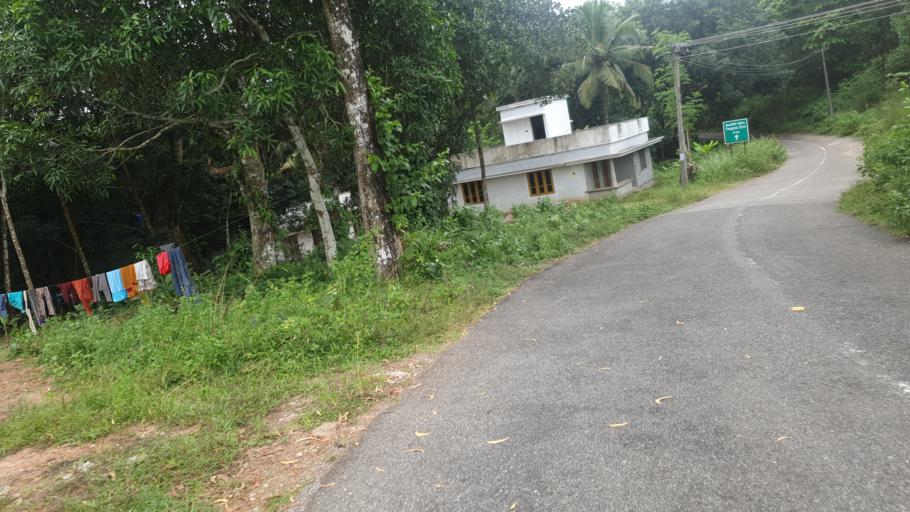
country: IN
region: Kerala
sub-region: Thiruvananthapuram
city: Nedumangad
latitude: 8.6385
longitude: 77.1094
